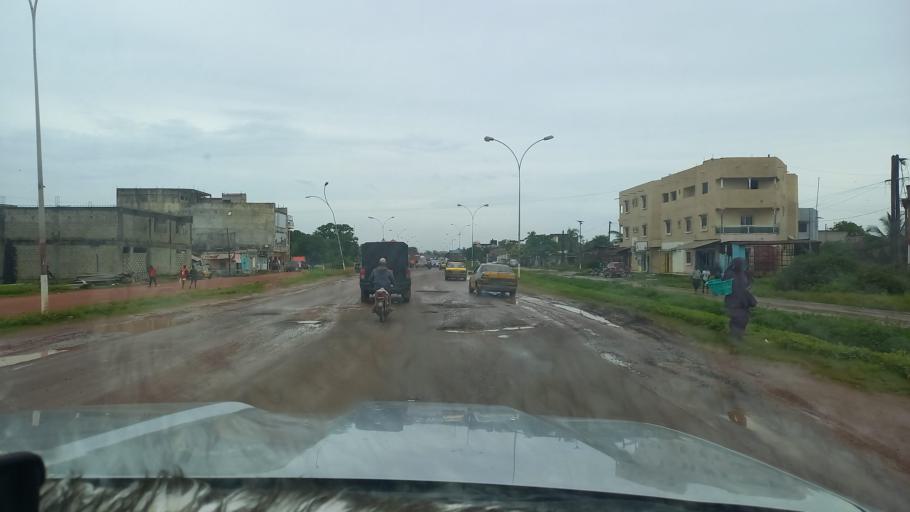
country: SN
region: Ziguinchor
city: Ziguinchor
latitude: 12.5756
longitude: -16.2693
